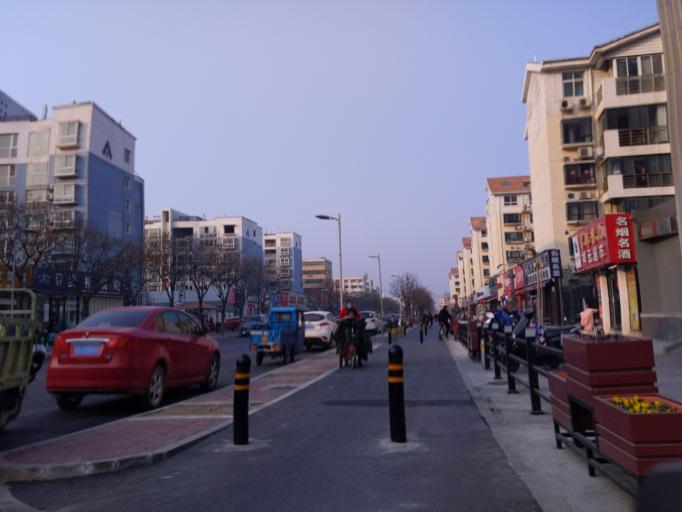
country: CN
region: Henan Sheng
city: Zhongyuanlu
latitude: 35.7742
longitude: 115.0650
